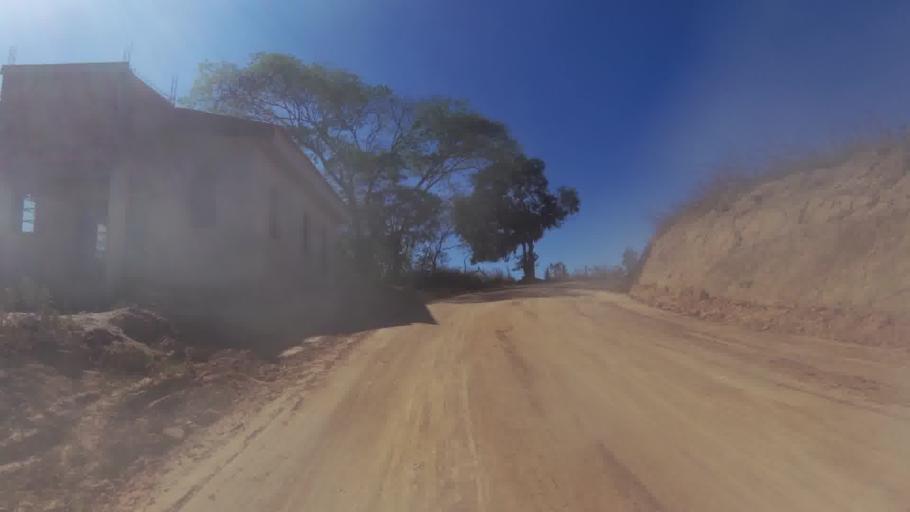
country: BR
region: Espirito Santo
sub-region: Marataizes
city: Marataizes
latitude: -21.1469
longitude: -40.9843
